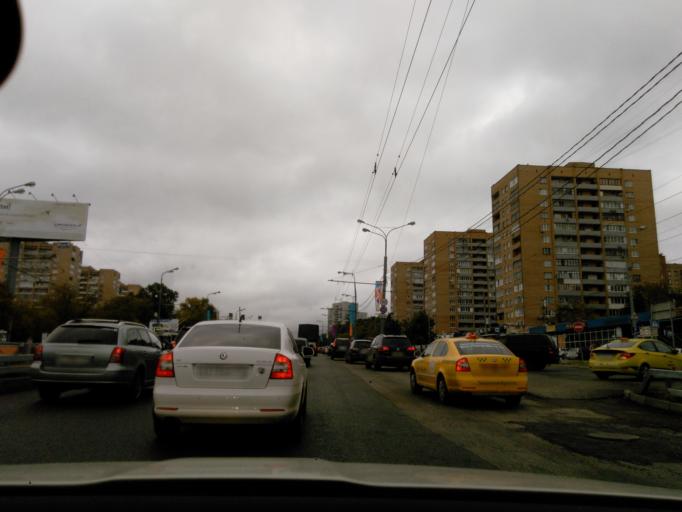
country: RU
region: Moscow
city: Pokrovskoye-Streshnevo
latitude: 55.8173
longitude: 37.4595
